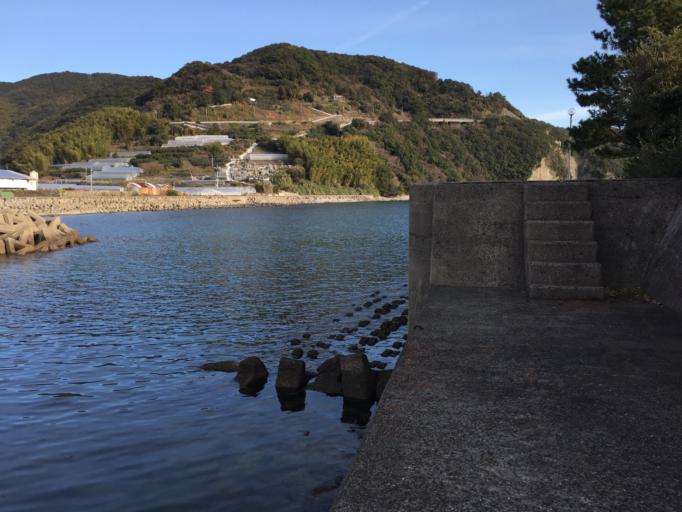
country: JP
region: Nagasaki
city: Nagasaki-shi
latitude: 32.7288
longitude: 129.9401
